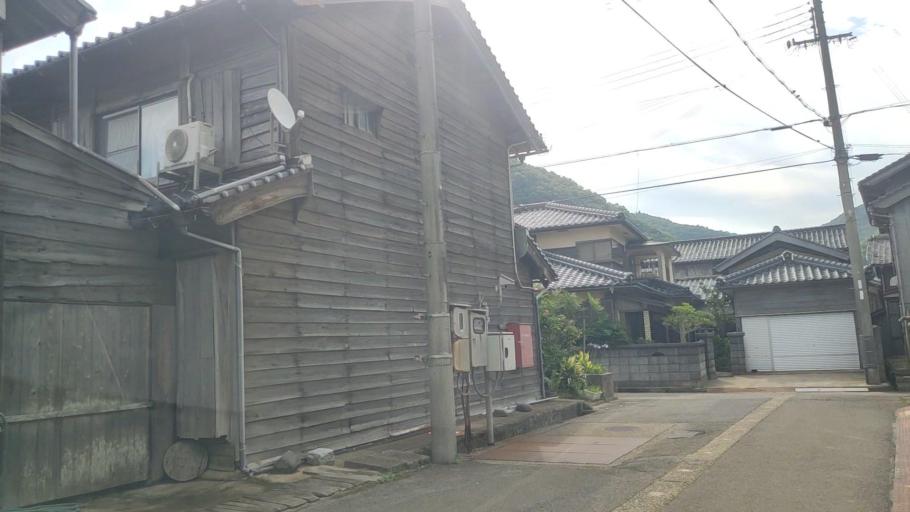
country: JP
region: Hyogo
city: Toyooka
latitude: 35.6437
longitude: 134.8443
